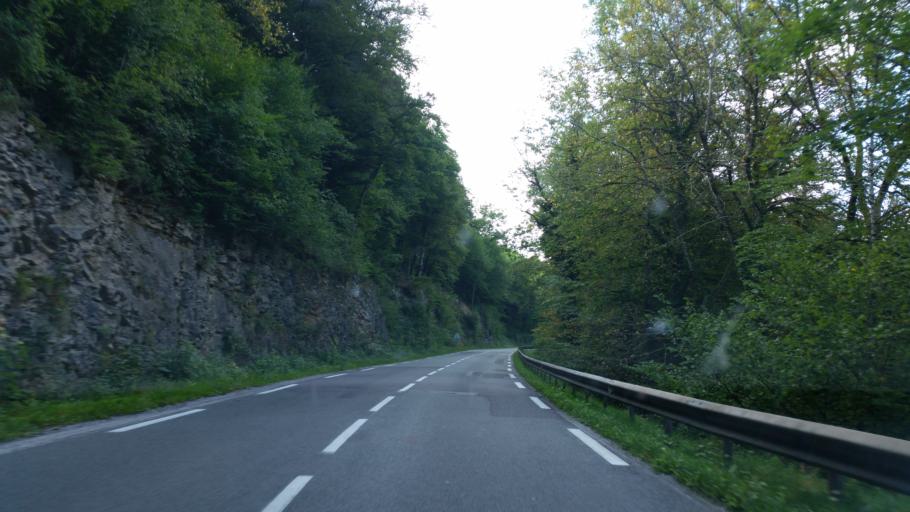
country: FR
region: Franche-Comte
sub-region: Departement du Doubs
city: Saint-Hippolyte
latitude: 47.3091
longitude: 6.8051
